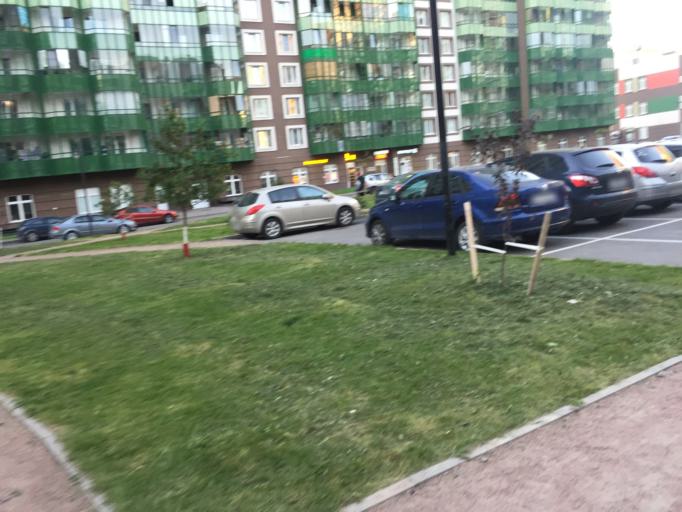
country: RU
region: Leningrad
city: Murino
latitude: 60.0576
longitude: 30.4253
